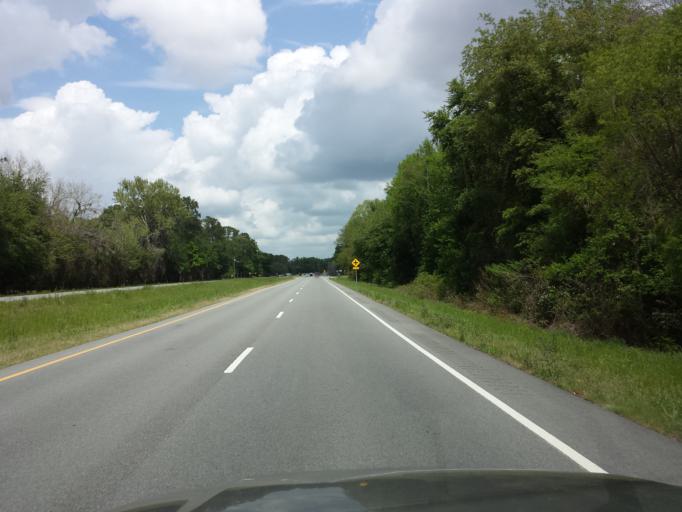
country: US
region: Georgia
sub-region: Lowndes County
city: Valdosta
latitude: 30.7453
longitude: -83.2192
